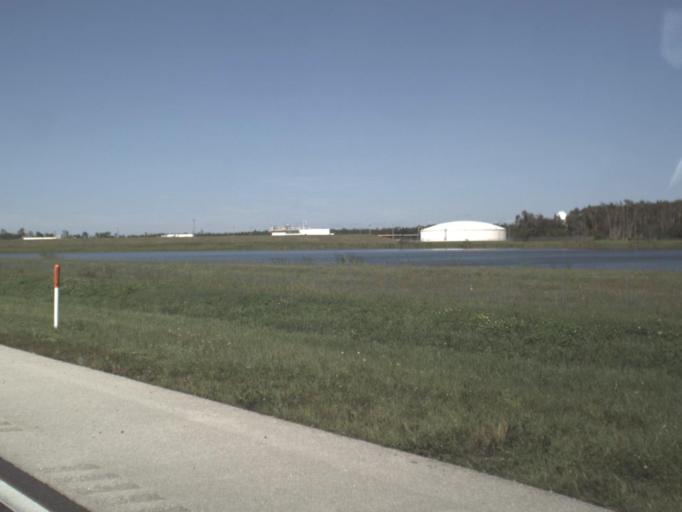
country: US
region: Florida
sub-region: Lee County
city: Bonita Springs
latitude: 26.3684
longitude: -81.7677
